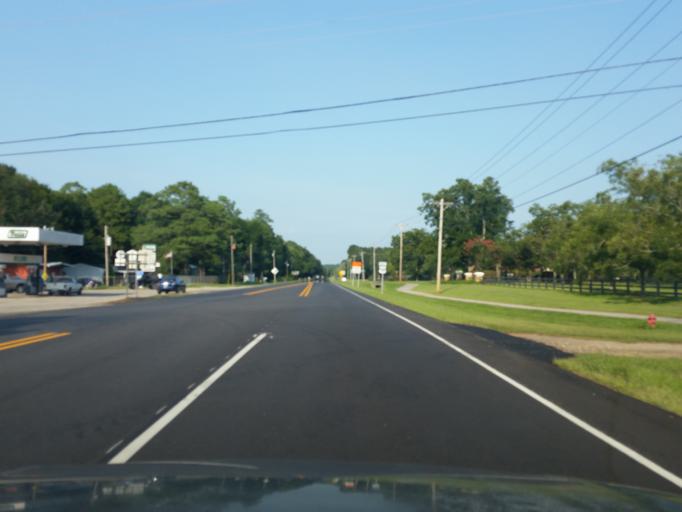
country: US
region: Alabama
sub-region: Baldwin County
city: Point Clear
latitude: 30.4188
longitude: -87.8439
